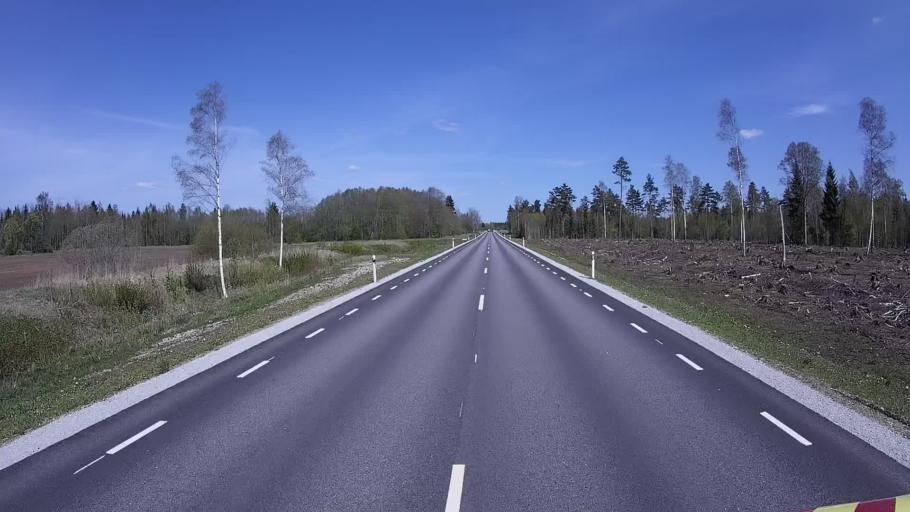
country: EE
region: Harju
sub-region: Nissi vald
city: Turba
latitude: 59.1749
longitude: 24.0779
